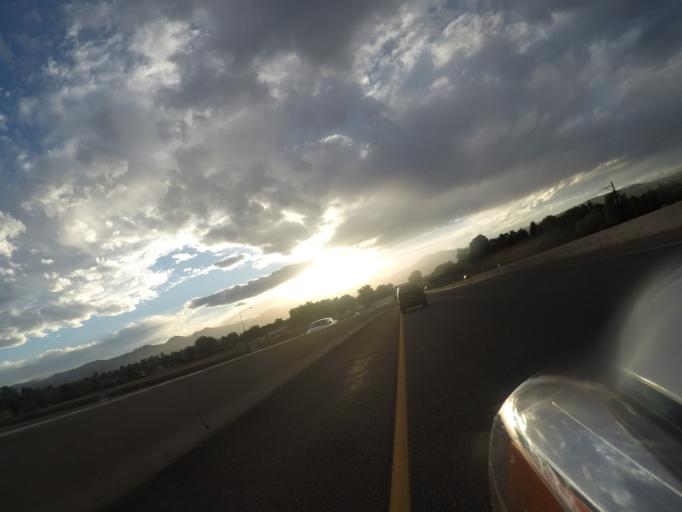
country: US
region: Colorado
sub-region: Jefferson County
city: Lakewood
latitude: 39.6529
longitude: -105.0831
